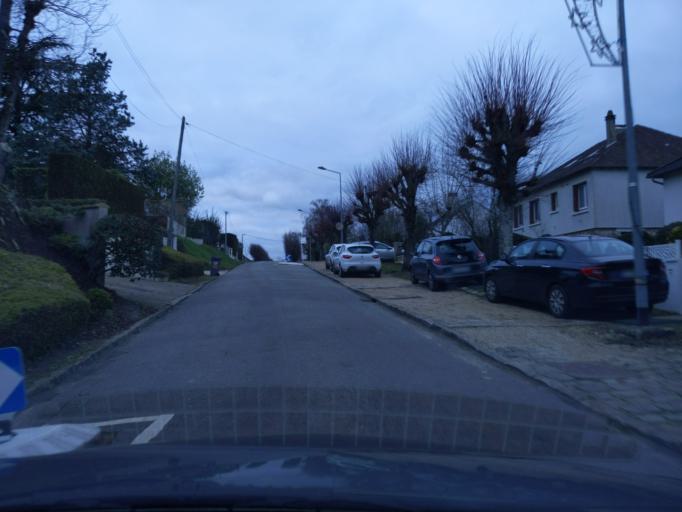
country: FR
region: Ile-de-France
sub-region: Departement des Yvelines
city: Saint-Remy-les-Chevreuse
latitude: 48.7080
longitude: 2.0659
